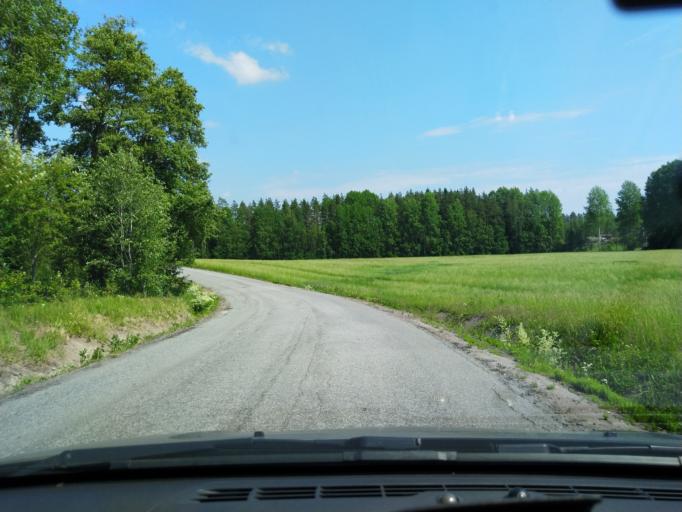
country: FI
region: Uusimaa
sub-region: Helsinki
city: Lohja
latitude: 60.3587
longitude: 24.0948
